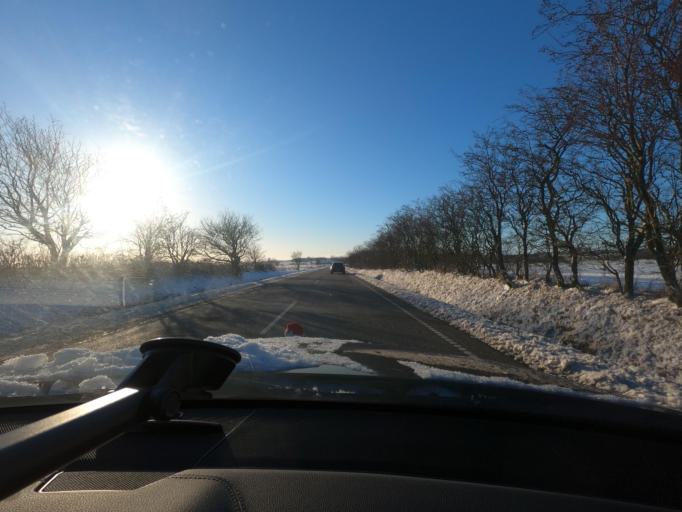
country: DK
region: South Denmark
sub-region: Tonder Kommune
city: Toftlund
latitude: 55.1743
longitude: 8.9928
